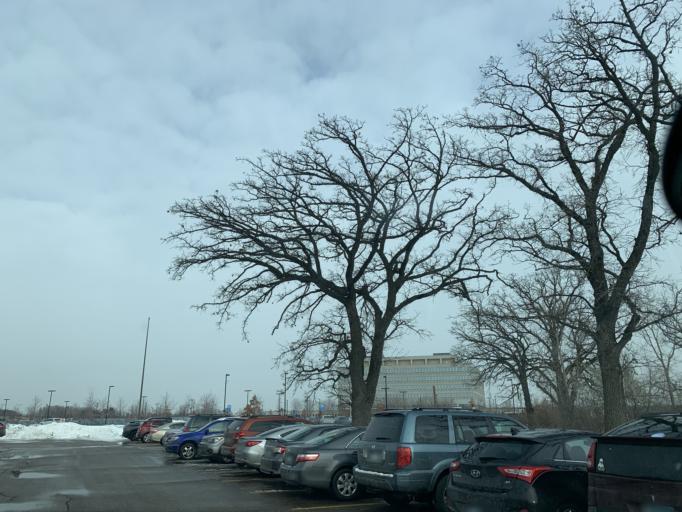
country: US
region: Minnesota
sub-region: Dakota County
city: Mendota Heights
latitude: 44.8917
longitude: -93.1967
